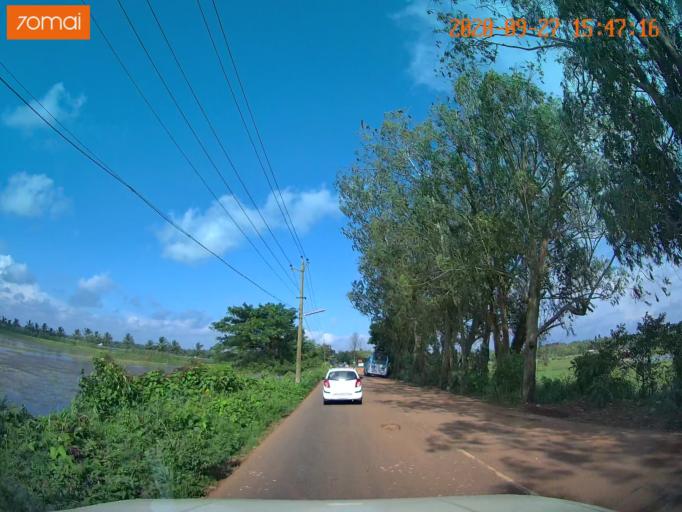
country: IN
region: Kerala
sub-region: Thrissur District
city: Thanniyam
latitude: 10.4817
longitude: 76.1277
